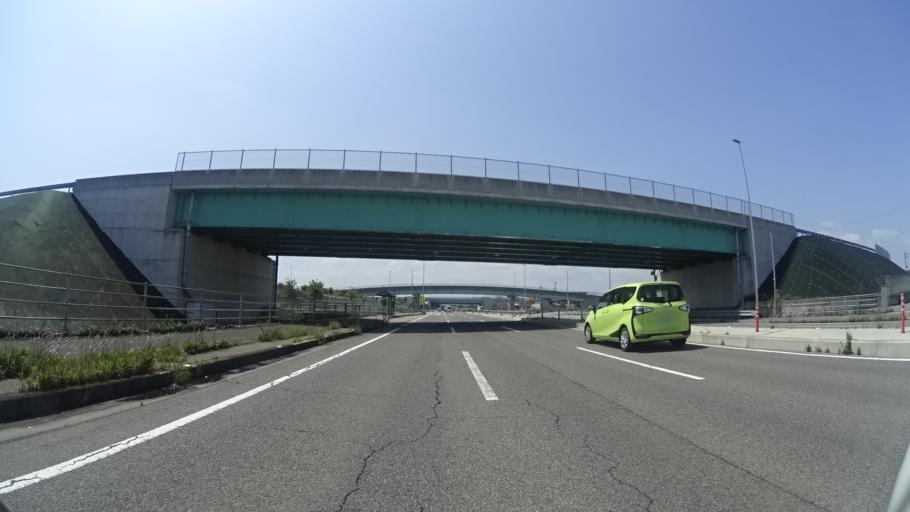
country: JP
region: Tokushima
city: Tokushima-shi
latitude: 34.1042
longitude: 134.5760
